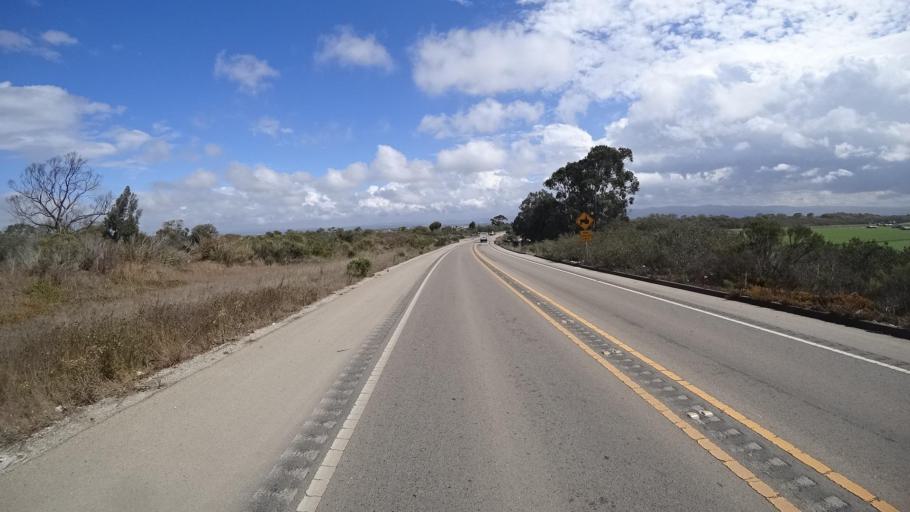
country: US
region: California
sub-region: Monterey County
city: Marina
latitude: 36.6768
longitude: -121.7496
